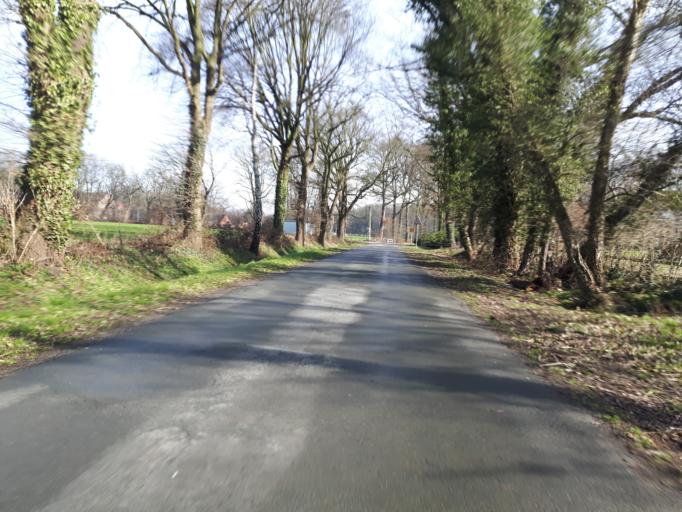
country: DE
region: North Rhine-Westphalia
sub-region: Regierungsbezirk Munster
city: Haltern
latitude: 51.7820
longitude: 7.2296
